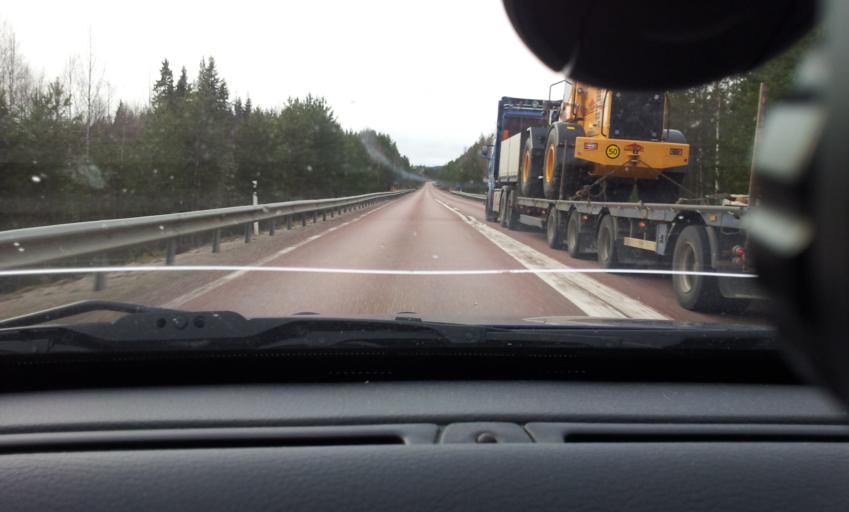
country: SE
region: Gaevleborg
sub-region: Ljusdals Kommun
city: Farila
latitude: 61.8088
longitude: 15.7741
